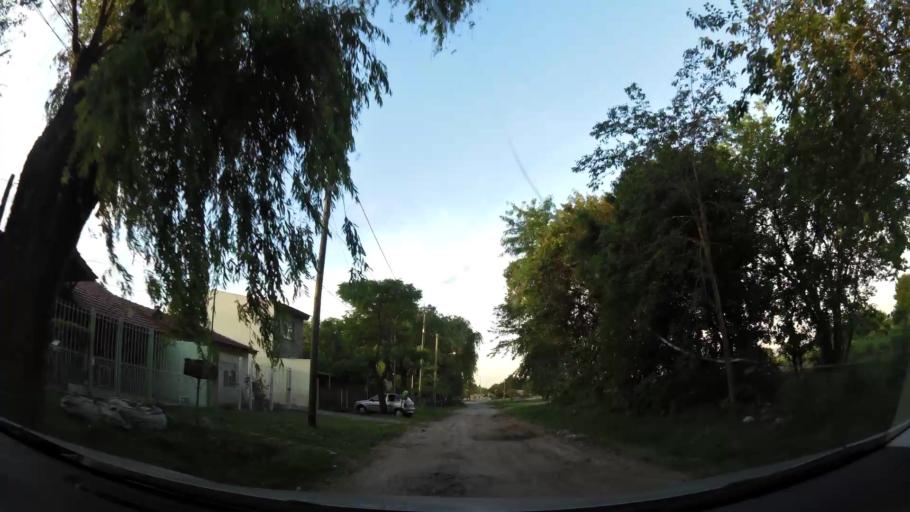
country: AR
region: Buenos Aires
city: Santa Catalina - Dique Lujan
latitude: -34.4419
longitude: -58.6602
